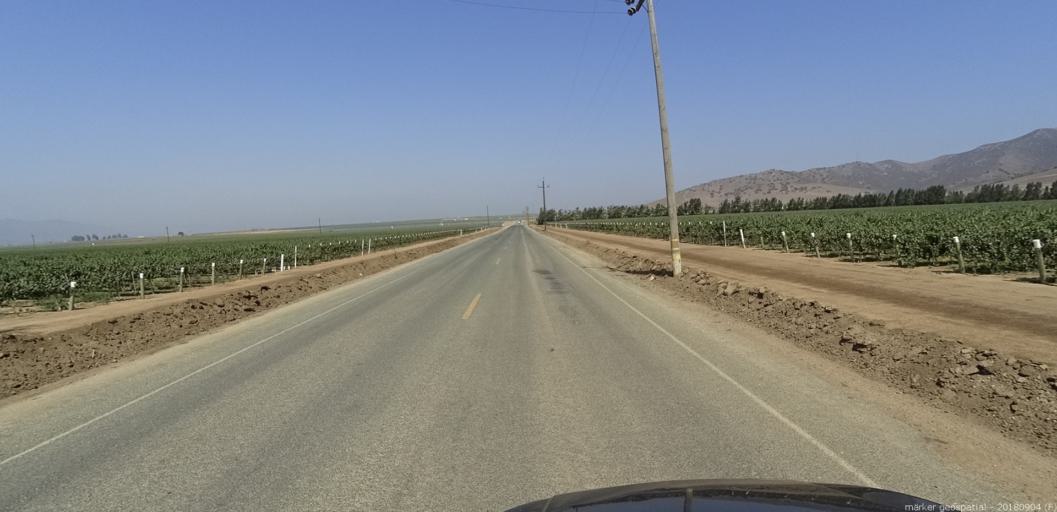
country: US
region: California
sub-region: Monterey County
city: Gonzales
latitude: 36.5537
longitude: -121.4435
